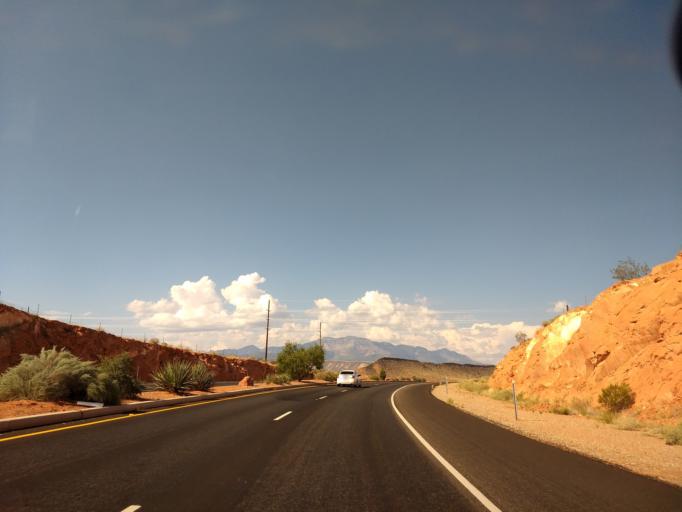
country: US
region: Utah
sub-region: Washington County
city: Saint George
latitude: 37.1243
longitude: -113.5840
